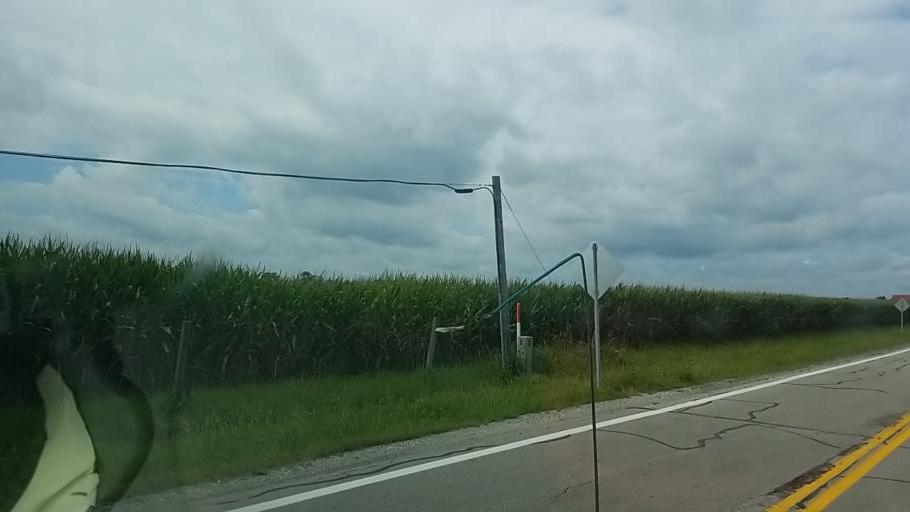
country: US
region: Ohio
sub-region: Fayette County
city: Jeffersonville
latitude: 39.6638
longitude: -83.5754
